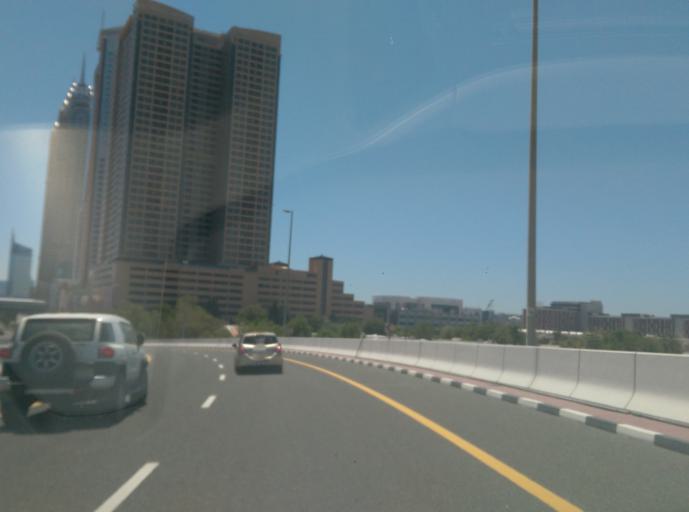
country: AE
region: Dubai
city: Dubai
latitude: 25.1044
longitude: 55.1751
